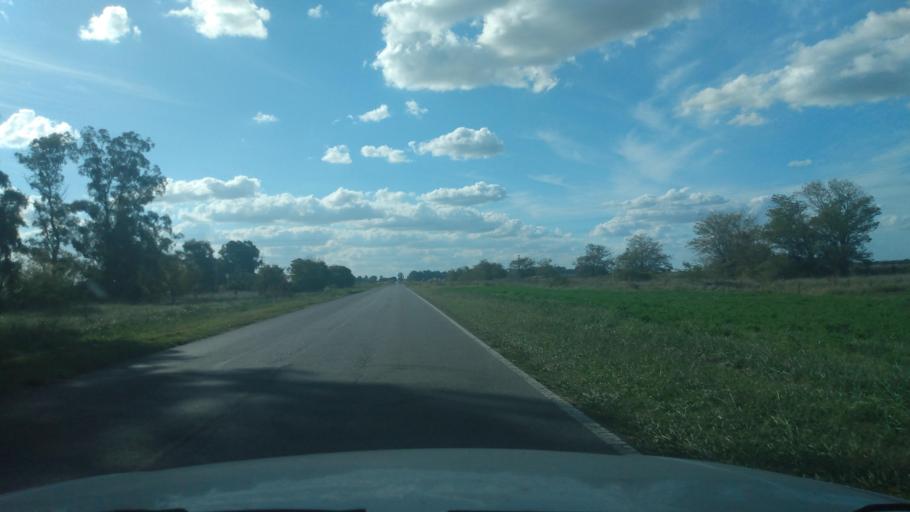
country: AR
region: Buenos Aires
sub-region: Partido de Navarro
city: Navarro
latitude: -34.9045
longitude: -59.3330
